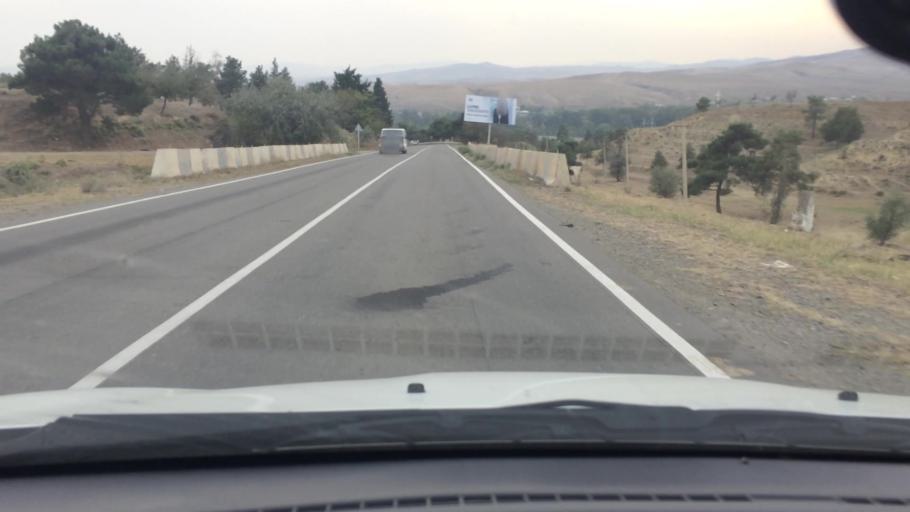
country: GE
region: Kvemo Kartli
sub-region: Gardabani
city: Gardabani
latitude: 41.3466
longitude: 45.0684
